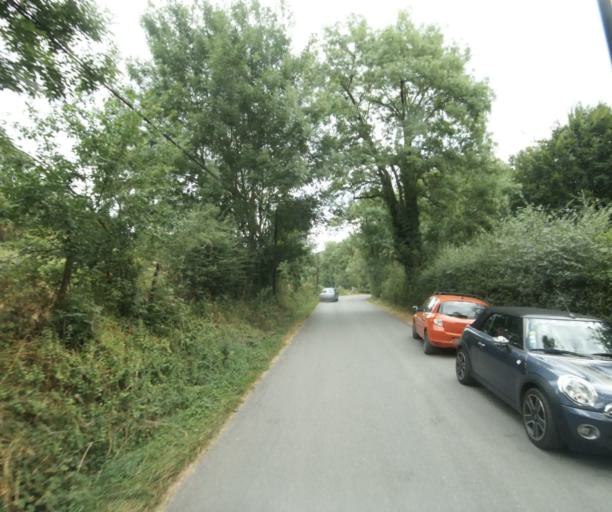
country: FR
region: Midi-Pyrenees
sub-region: Departement du Tarn
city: Soreze
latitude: 43.4349
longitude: 2.0402
